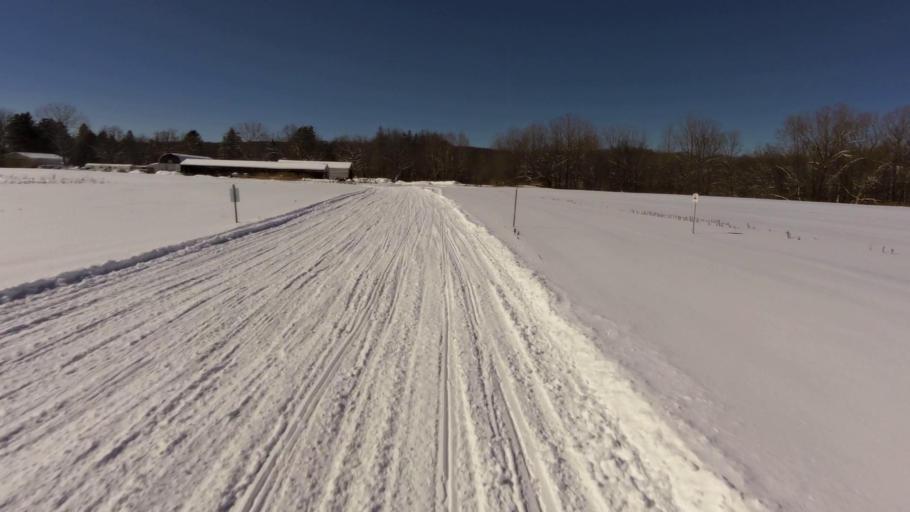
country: US
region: New York
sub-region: Chautauqua County
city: Mayville
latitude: 42.2477
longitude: -79.4357
